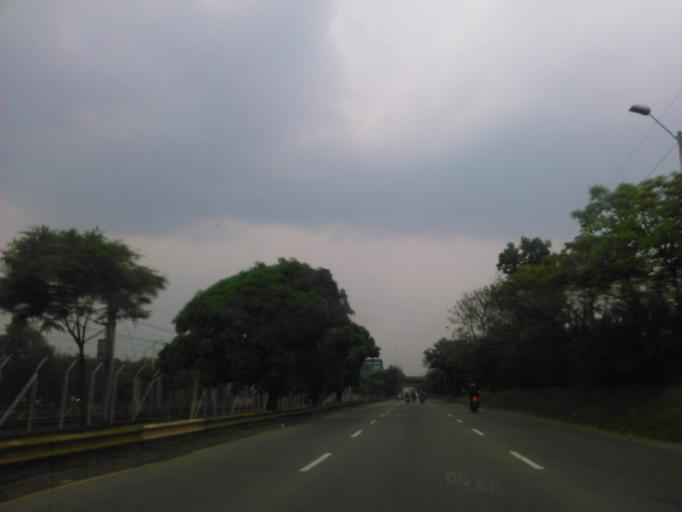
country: CO
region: Antioquia
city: Itagui
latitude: 6.2104
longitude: -75.5782
